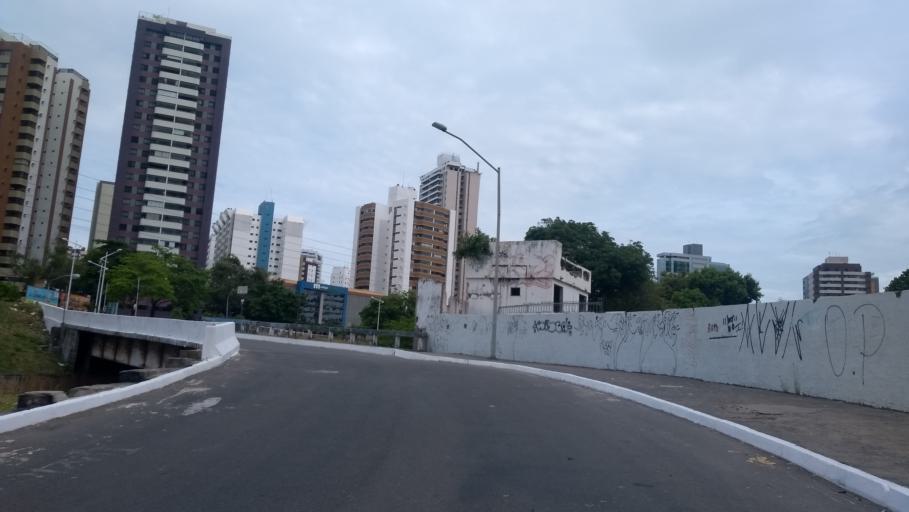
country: BR
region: Bahia
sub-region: Salvador
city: Salvador
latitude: -12.9910
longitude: -38.4493
